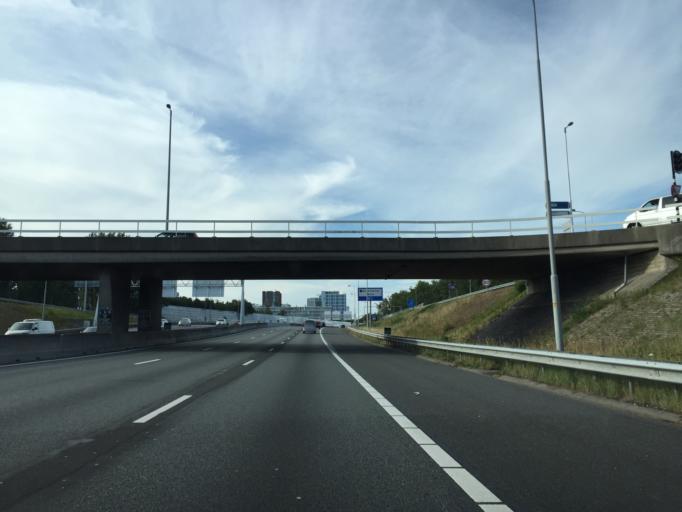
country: NL
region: North Holland
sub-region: Gemeente Amstelveen
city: Amstelveen
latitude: 52.3456
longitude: 4.8412
